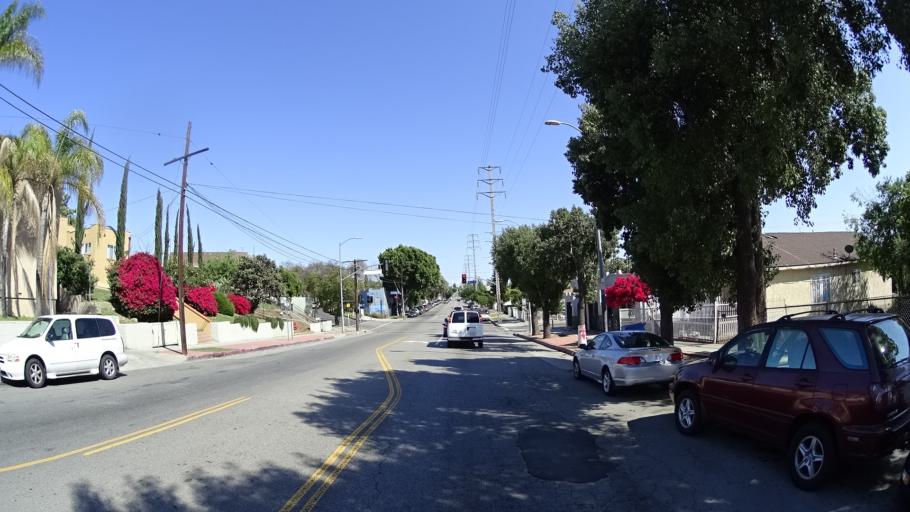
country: US
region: California
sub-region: Los Angeles County
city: Boyle Heights
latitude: 34.0516
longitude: -118.2006
